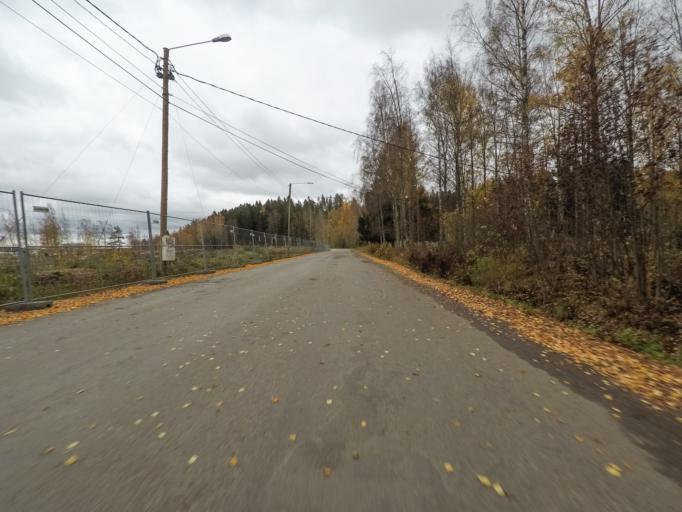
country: FI
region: Uusimaa
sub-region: Porvoo
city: Porvoo
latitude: 60.3857
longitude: 25.6614
